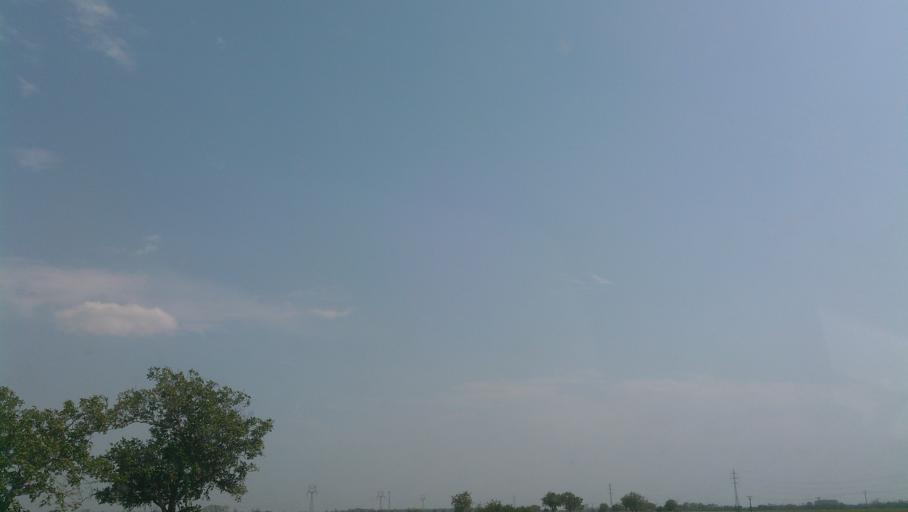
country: SK
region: Trnavsky
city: Samorin
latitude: 48.0732
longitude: 17.3994
